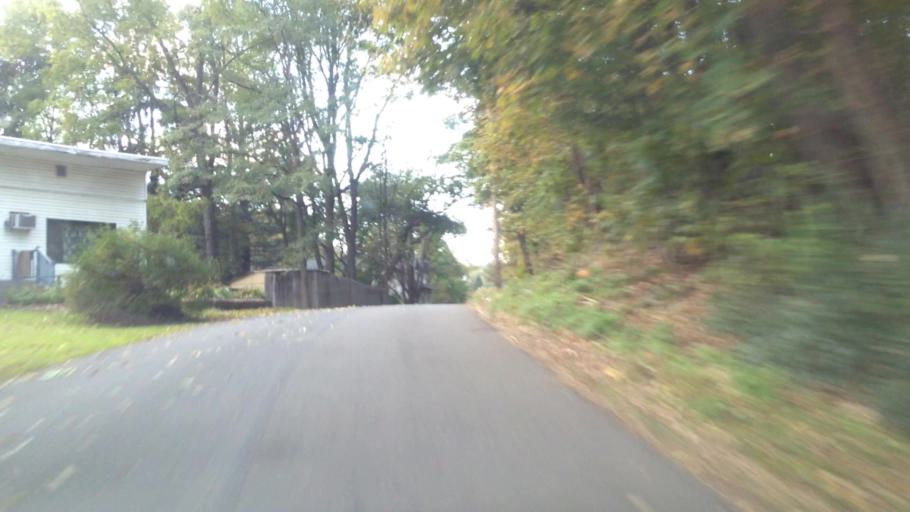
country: US
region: New York
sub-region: Dutchess County
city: Hyde Park
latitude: 41.7953
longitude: -73.9608
